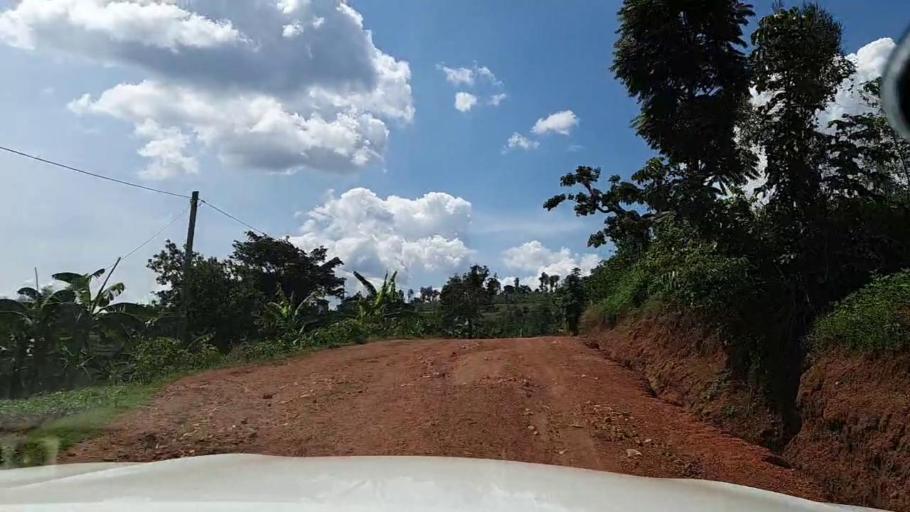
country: RW
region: Southern Province
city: Butare
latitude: -2.7463
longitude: 29.7042
